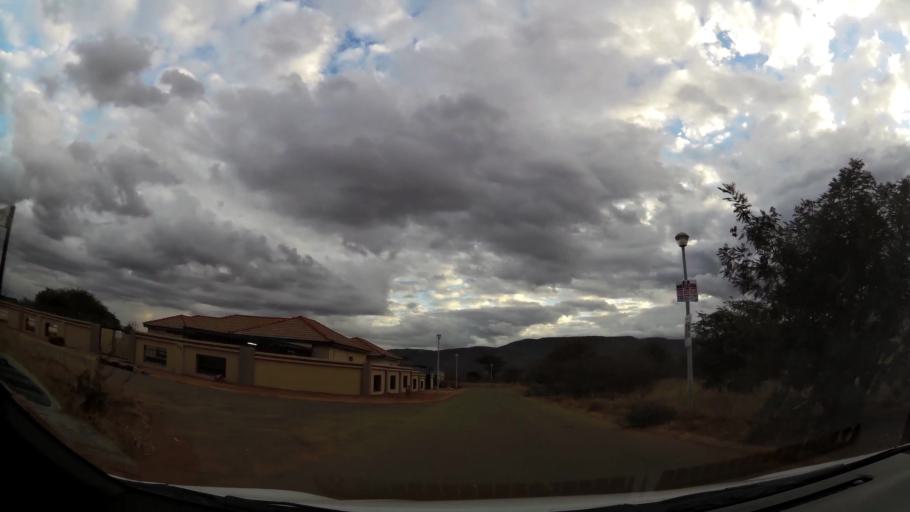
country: ZA
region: Limpopo
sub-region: Waterberg District Municipality
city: Mokopane
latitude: -24.1983
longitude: 29.0006
